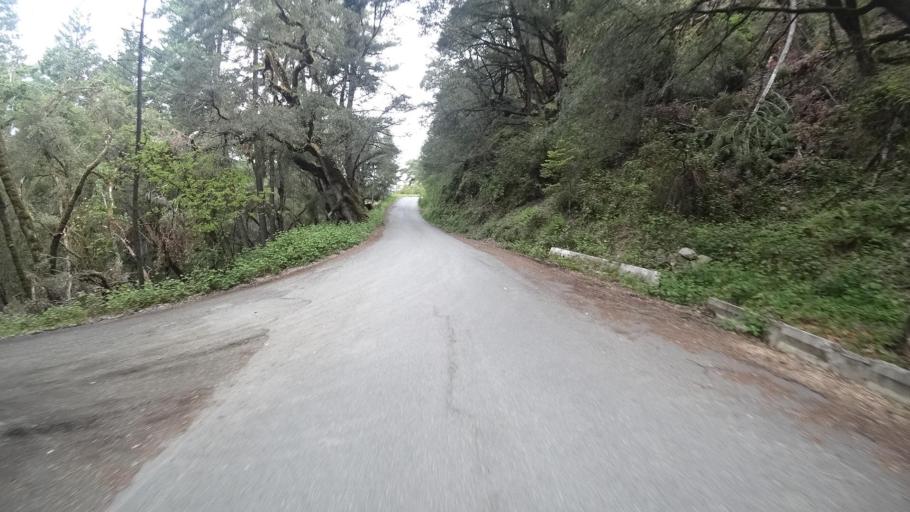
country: US
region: California
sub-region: Humboldt County
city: Willow Creek
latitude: 40.9334
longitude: -123.6154
